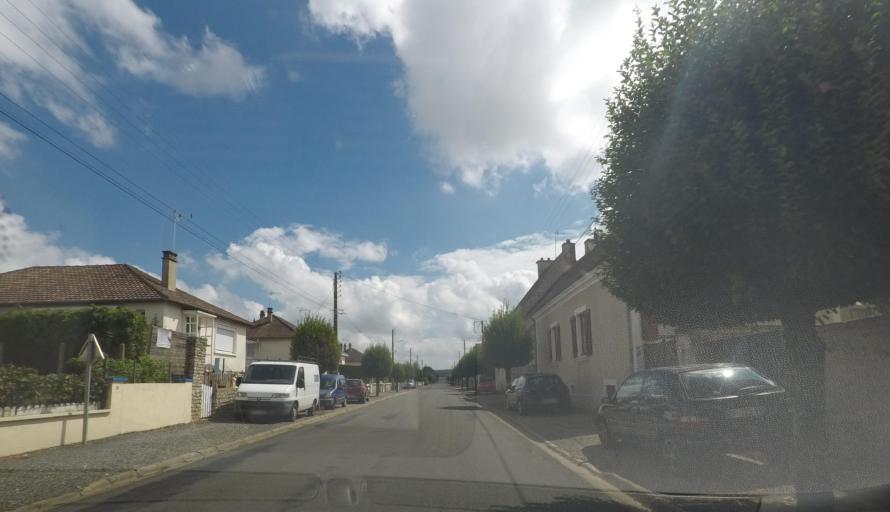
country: FR
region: Pays de la Loire
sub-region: Departement de la Sarthe
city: Saint-Cosme-en-Vairais
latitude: 48.2727
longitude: 0.4653
